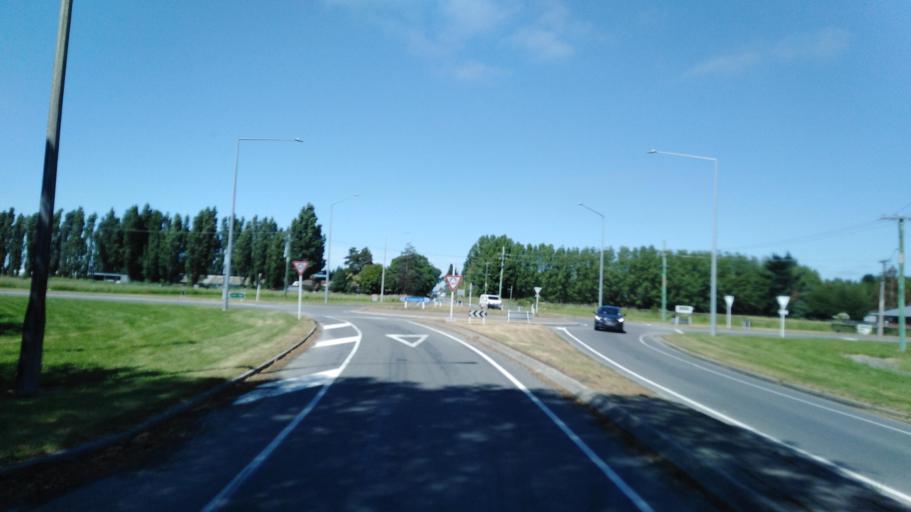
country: NZ
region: Canterbury
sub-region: Selwyn District
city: Prebbleton
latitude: -43.5190
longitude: 172.5052
